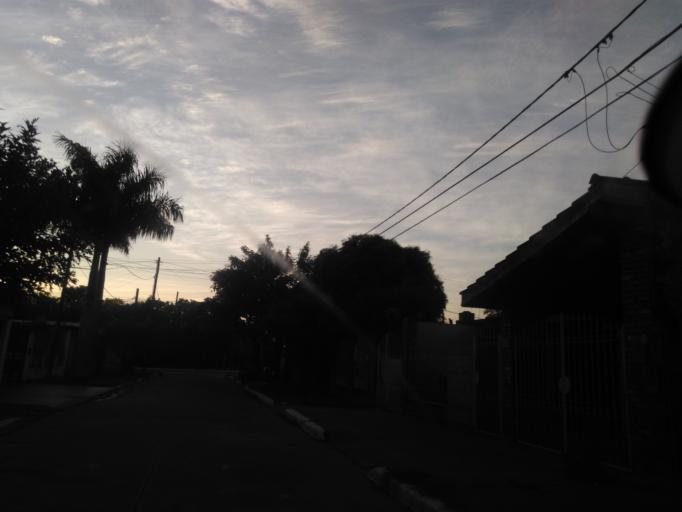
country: AR
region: Chaco
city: Resistencia
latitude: -27.4524
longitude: -59.0157
